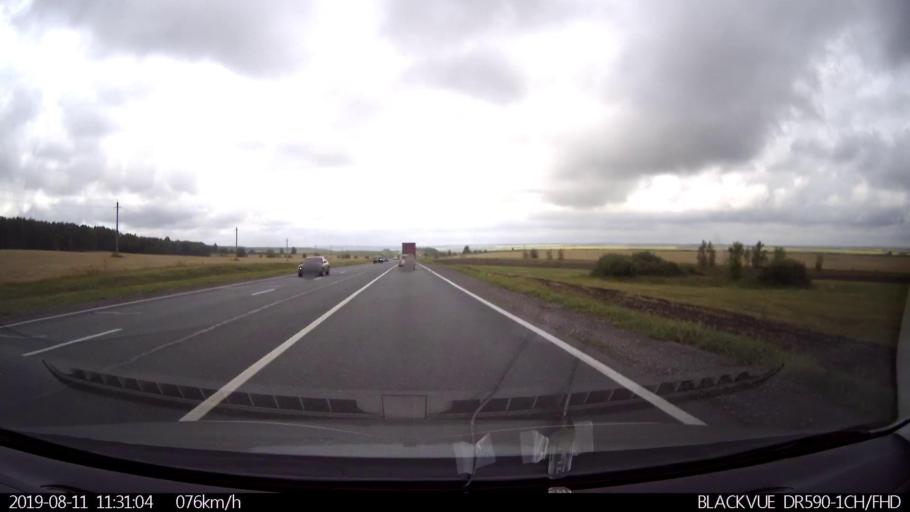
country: RU
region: Ulyanovsk
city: Krasnyy Gulyay
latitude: 54.0512
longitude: 48.2170
